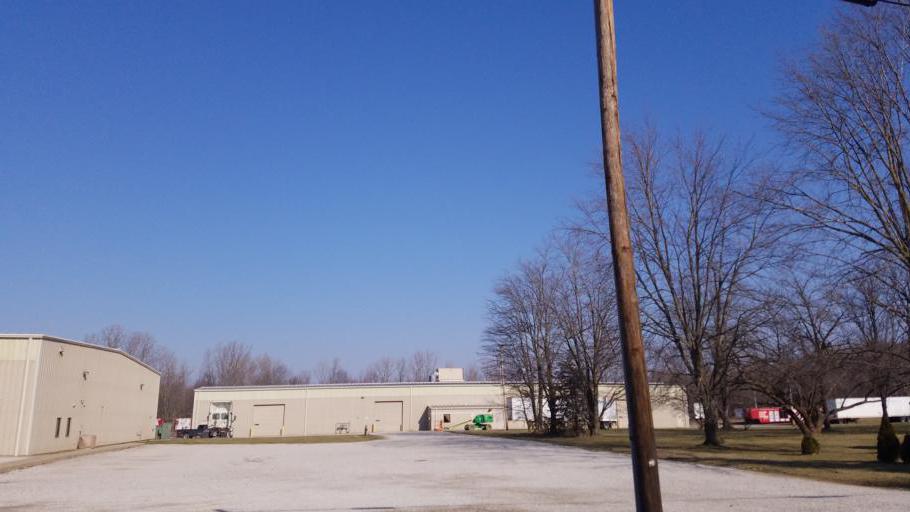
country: US
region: Ohio
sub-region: Crawford County
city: Galion
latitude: 40.7122
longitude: -82.7908
